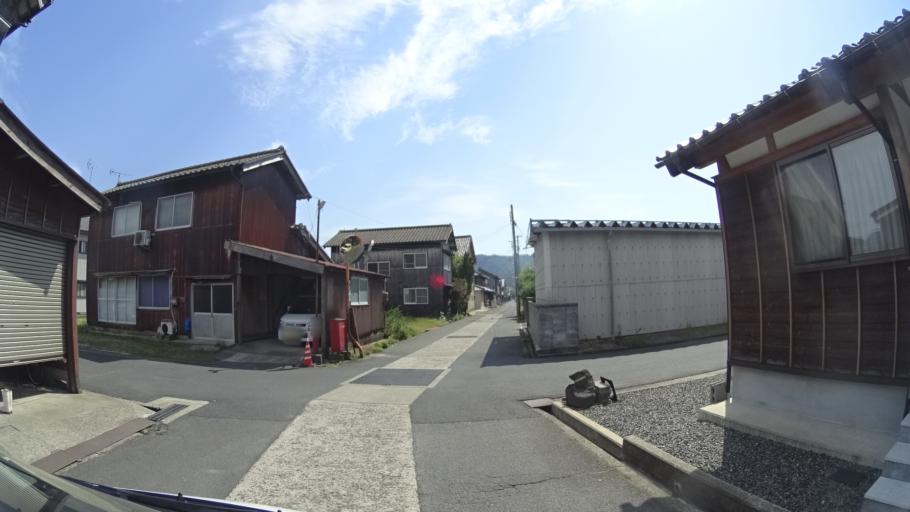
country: JP
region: Kyoto
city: Miyazu
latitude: 35.6874
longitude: 135.0287
